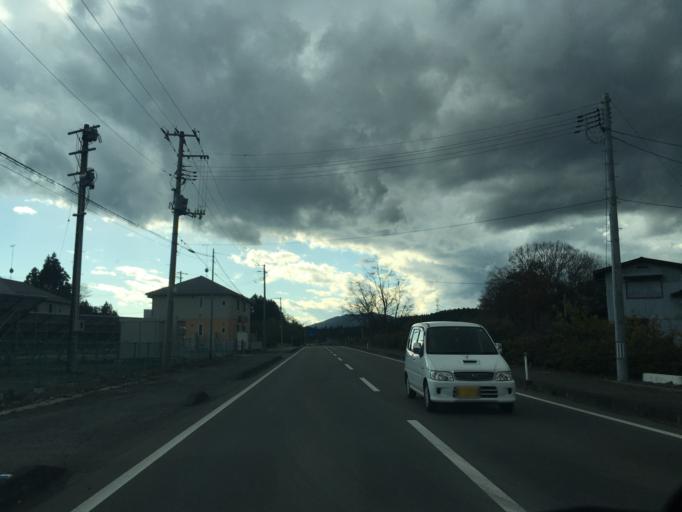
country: JP
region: Fukushima
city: Ishikawa
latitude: 37.0463
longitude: 140.3851
